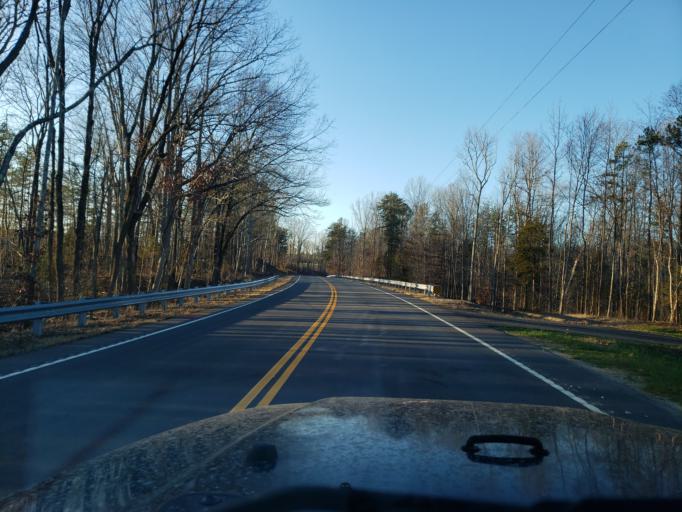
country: US
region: South Carolina
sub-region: Cherokee County
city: Blacksburg
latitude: 35.0285
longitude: -81.4032
